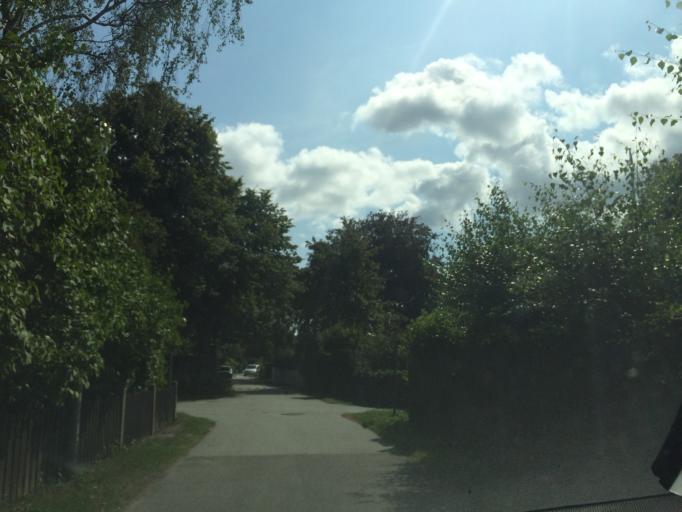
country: SE
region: Skane
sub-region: Vellinge Kommun
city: Skanor med Falsterbo
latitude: 55.3963
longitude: 12.8329
